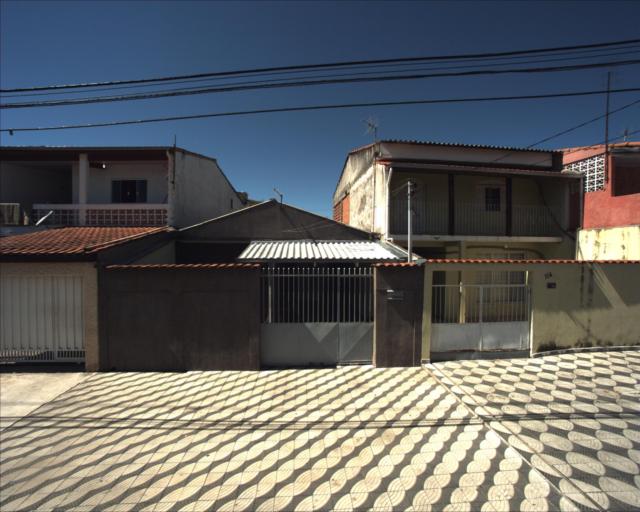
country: BR
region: Sao Paulo
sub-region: Votorantim
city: Votorantim
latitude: -23.5231
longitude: -47.4344
